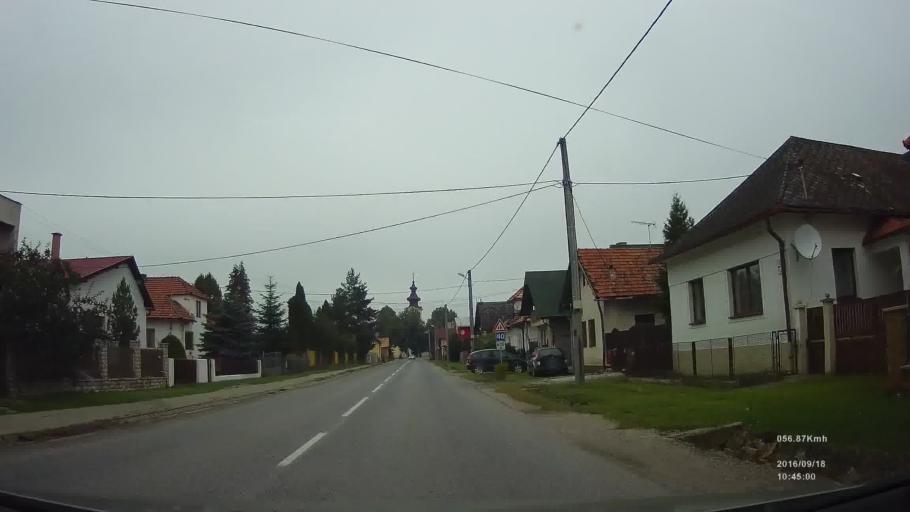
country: SK
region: Kosicky
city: Spisska Nova Ves
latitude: 48.9597
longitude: 20.5824
